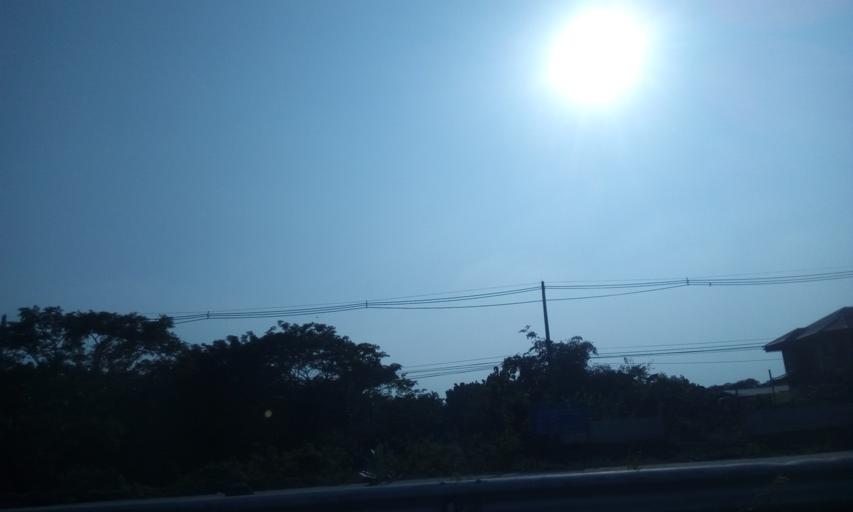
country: TH
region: Sing Buri
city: Sing Buri
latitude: 14.8503
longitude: 100.4149
